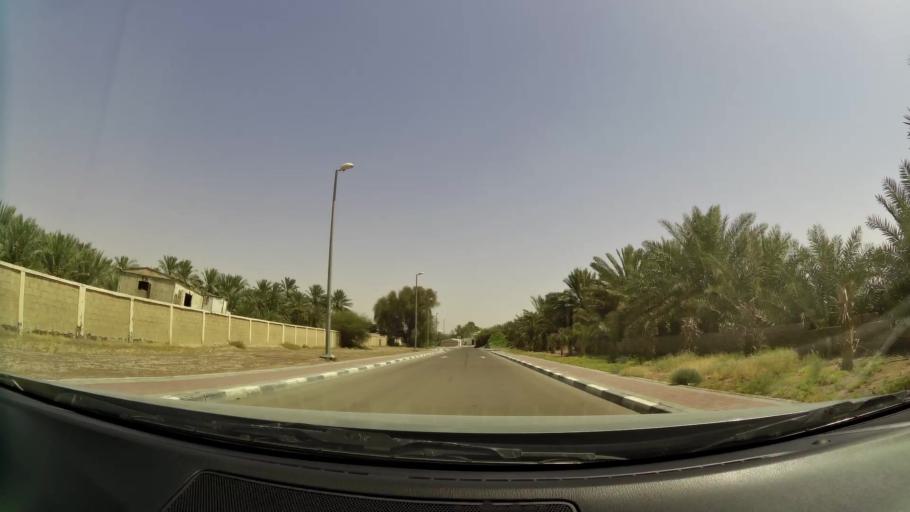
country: OM
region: Al Buraimi
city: Al Buraymi
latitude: 24.2772
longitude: 55.7805
